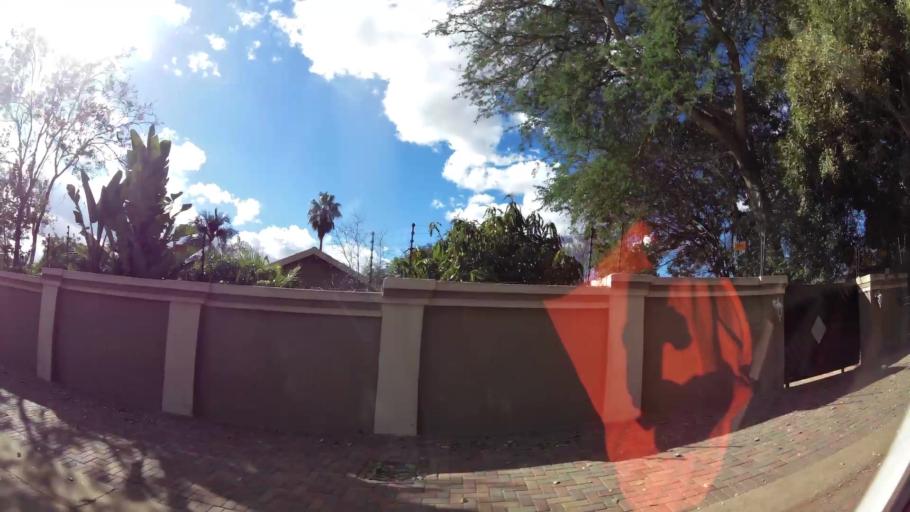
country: ZA
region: Limpopo
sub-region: Capricorn District Municipality
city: Polokwane
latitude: -23.8920
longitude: 29.4673
